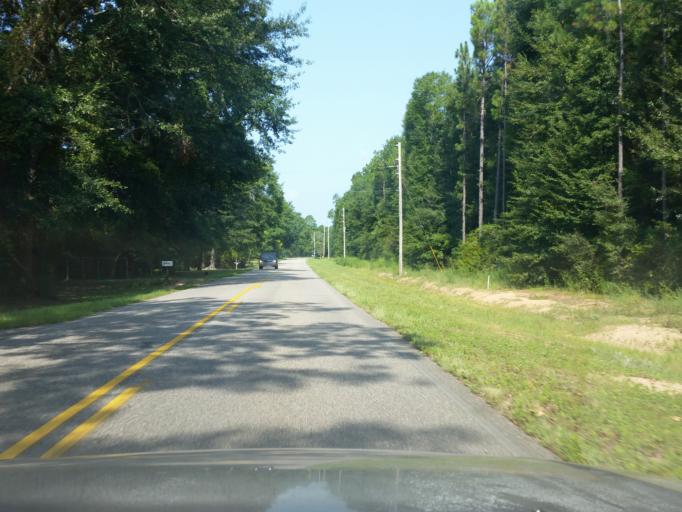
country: US
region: Florida
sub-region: Escambia County
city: Cantonment
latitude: 30.5118
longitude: -87.4656
